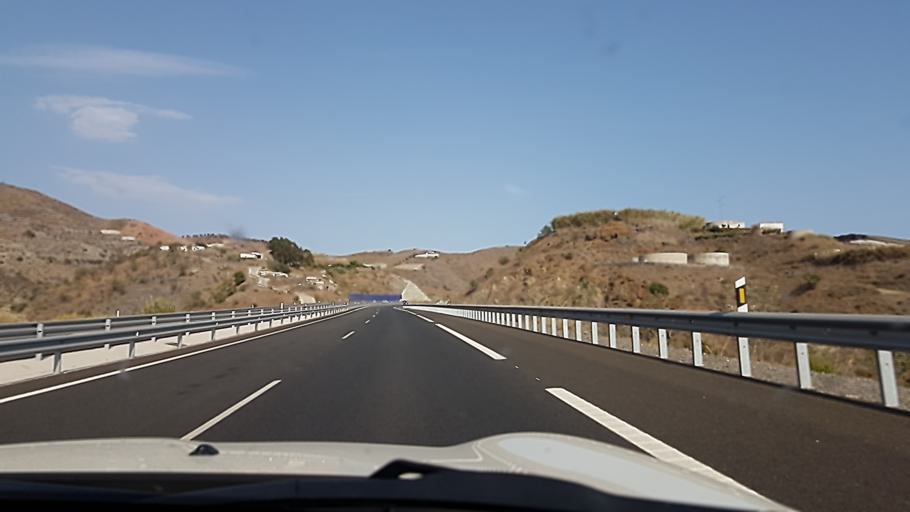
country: ES
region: Andalusia
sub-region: Provincia de Granada
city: Albunol
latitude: 36.7557
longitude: -3.2279
